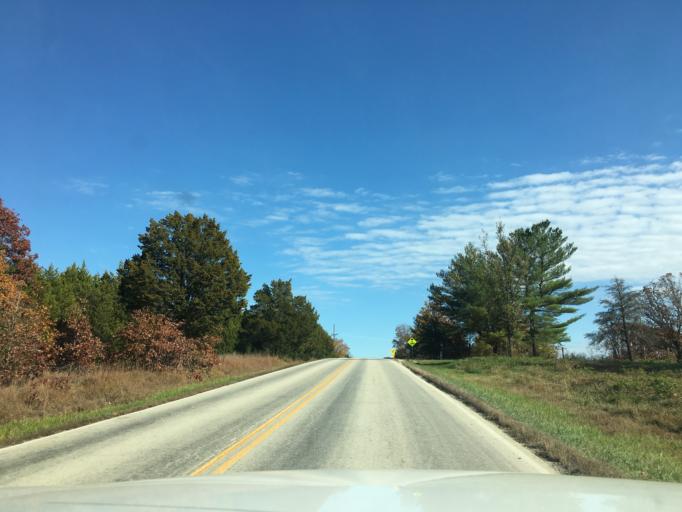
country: US
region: Missouri
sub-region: Maries County
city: Belle
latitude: 38.3039
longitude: -91.7329
